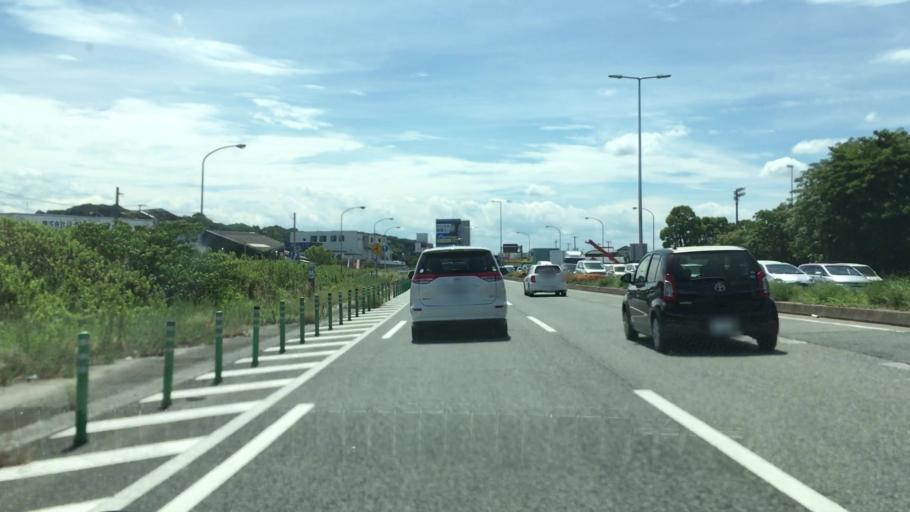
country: JP
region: Fukuoka
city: Onojo
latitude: 33.5306
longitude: 130.4923
